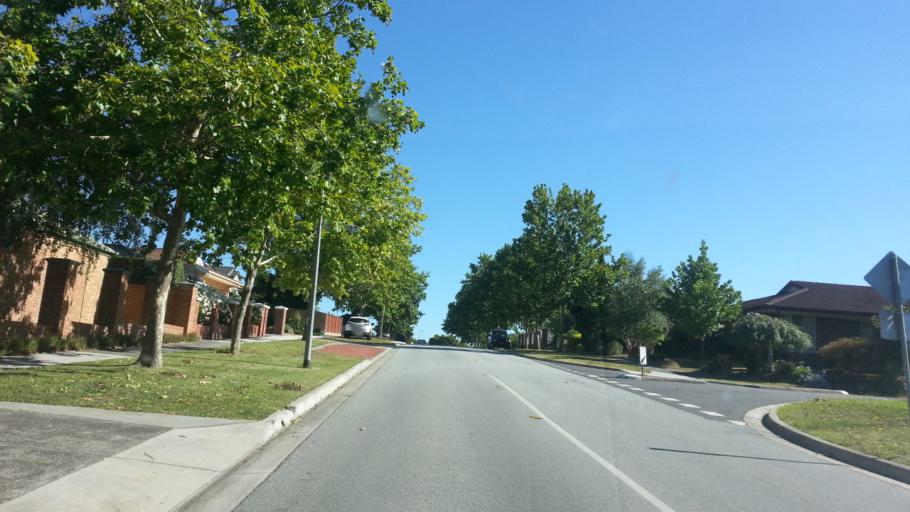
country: AU
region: Victoria
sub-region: Knox
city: Rowville
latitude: -37.9242
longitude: 145.2537
